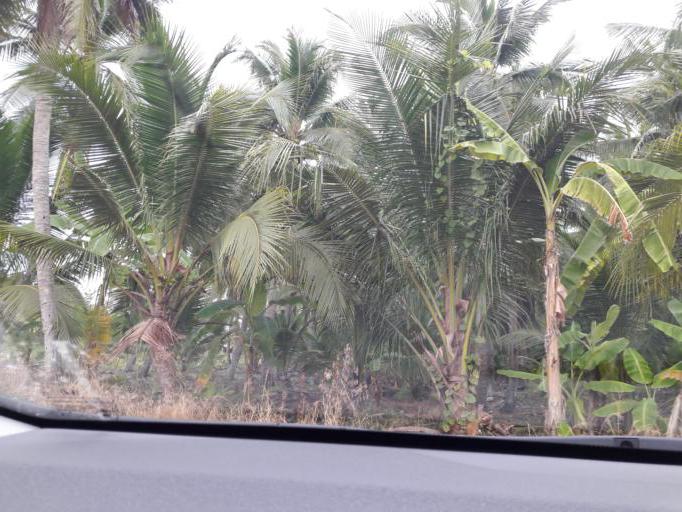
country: TH
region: Samut Sakhon
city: Ban Phaeo
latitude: 13.5417
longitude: 100.0435
